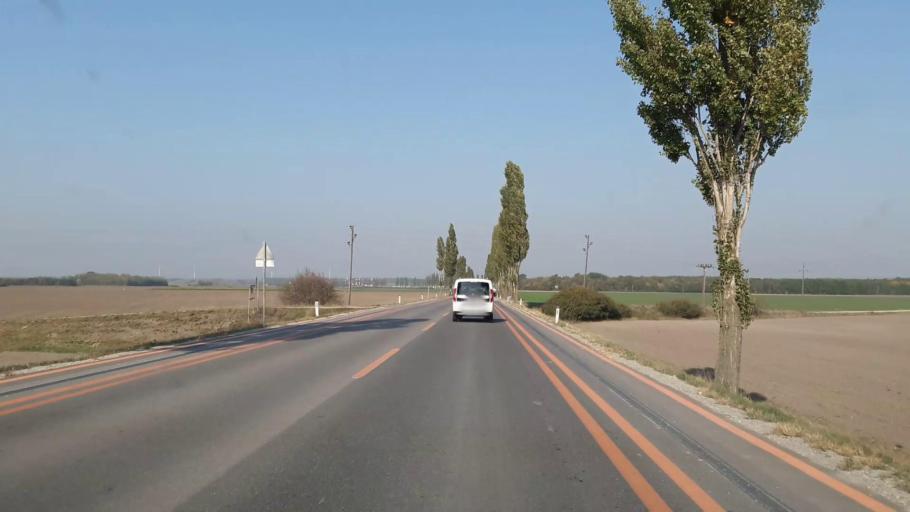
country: AT
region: Lower Austria
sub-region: Politischer Bezirk Ganserndorf
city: Engelhartstetten
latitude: 48.1886
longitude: 16.8960
